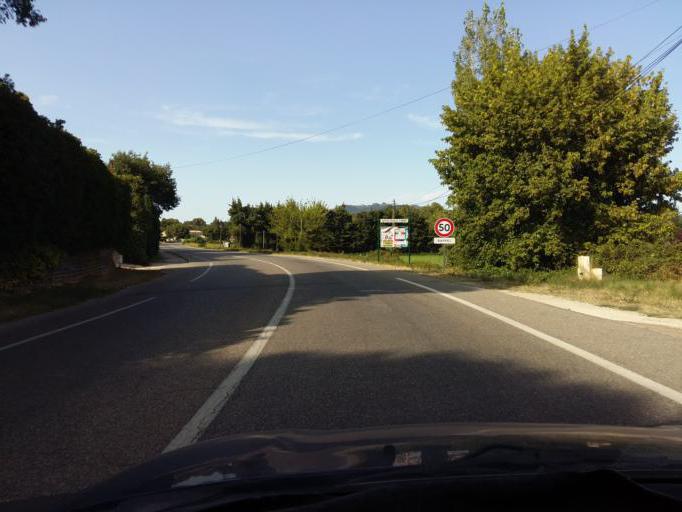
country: FR
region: Provence-Alpes-Cote d'Azur
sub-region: Departement du Vaucluse
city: Sarrians
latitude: 44.0885
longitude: 4.9716
